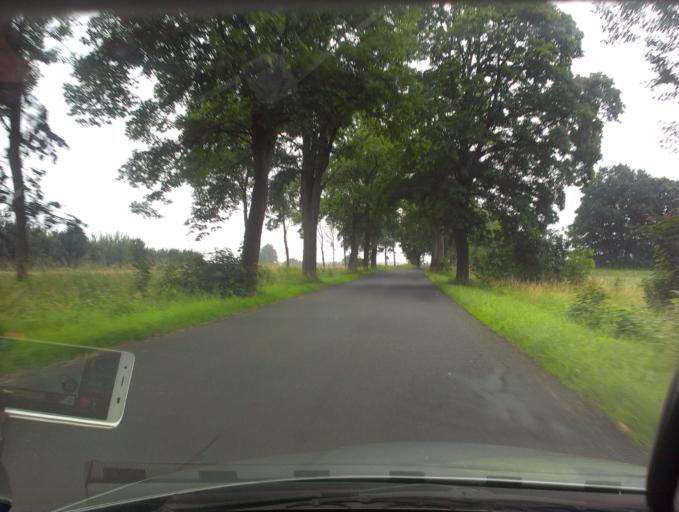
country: PL
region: West Pomeranian Voivodeship
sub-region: Powiat szczecinecki
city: Barwice
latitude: 53.7675
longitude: 16.3837
